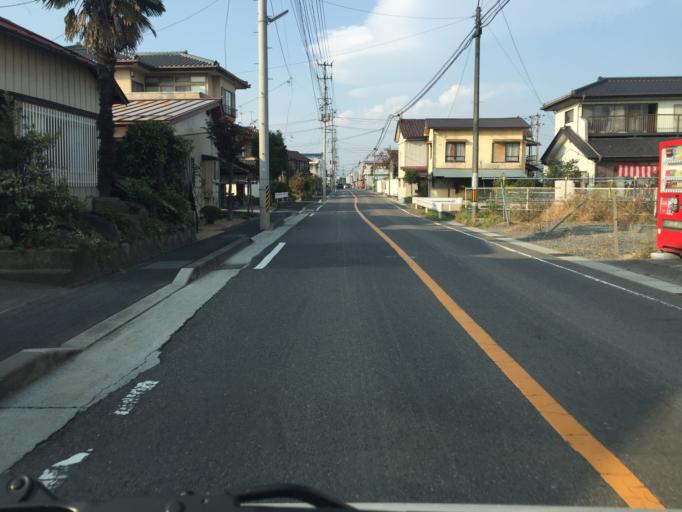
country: JP
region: Fukushima
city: Motomiya
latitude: 37.5072
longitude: 140.4011
